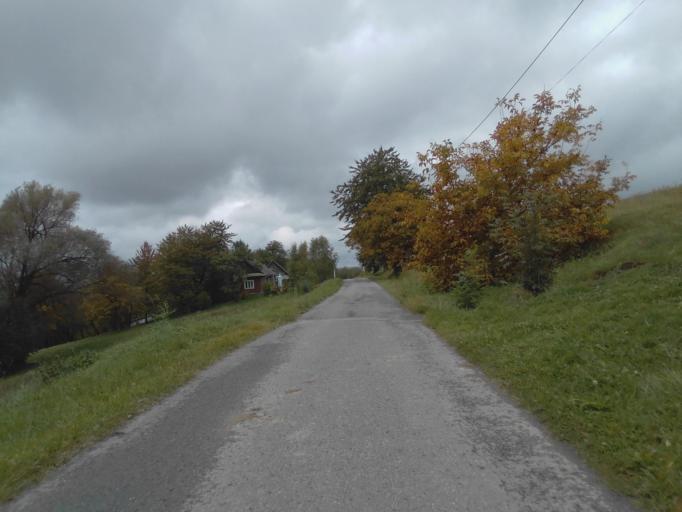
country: PL
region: Subcarpathian Voivodeship
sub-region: Powiat strzyzowski
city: Gwoznica Gorna
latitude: 49.8340
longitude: 22.0172
